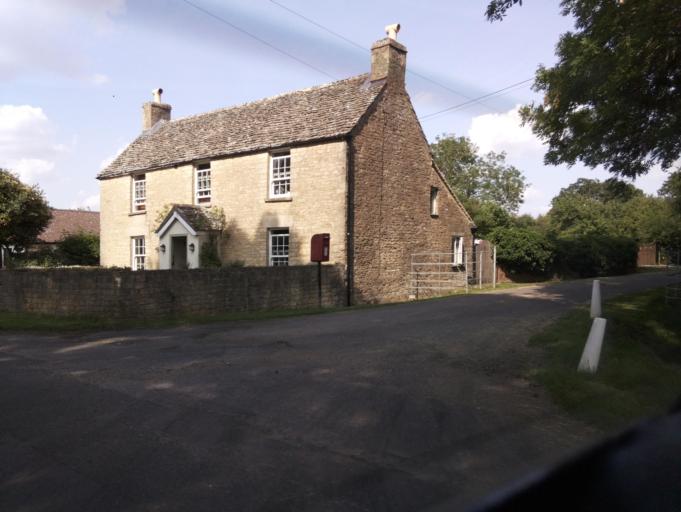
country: GB
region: England
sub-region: Wiltshire
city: Minety
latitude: 51.6356
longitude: -1.9760
